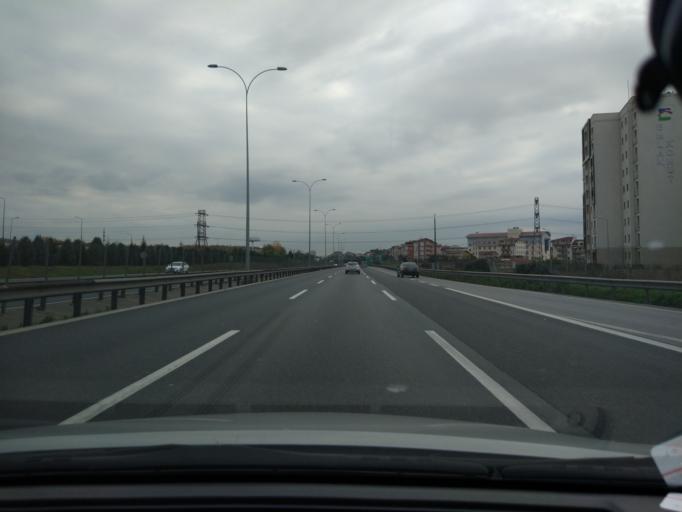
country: TR
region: Kocaeli
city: Derince
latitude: 40.7690
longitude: 29.8020
